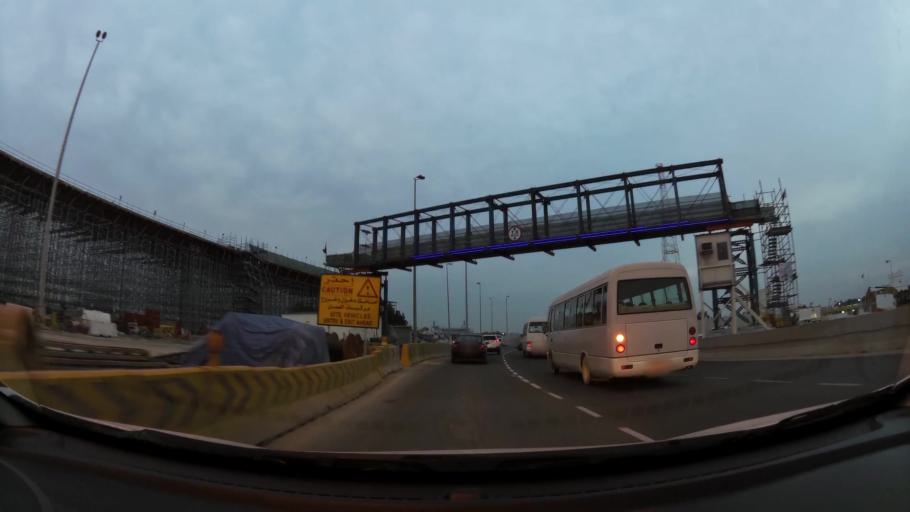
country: BH
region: Northern
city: Ar Rifa'
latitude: 26.1230
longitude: 50.5920
